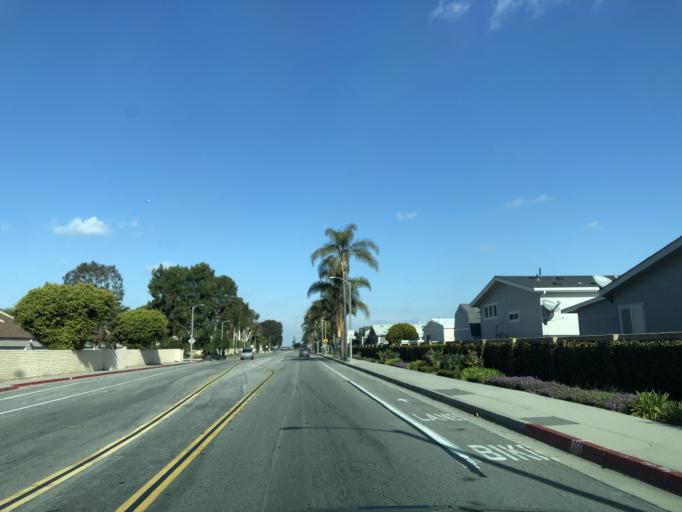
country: US
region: California
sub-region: Orange County
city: Seal Beach
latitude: 33.7227
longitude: -118.0545
